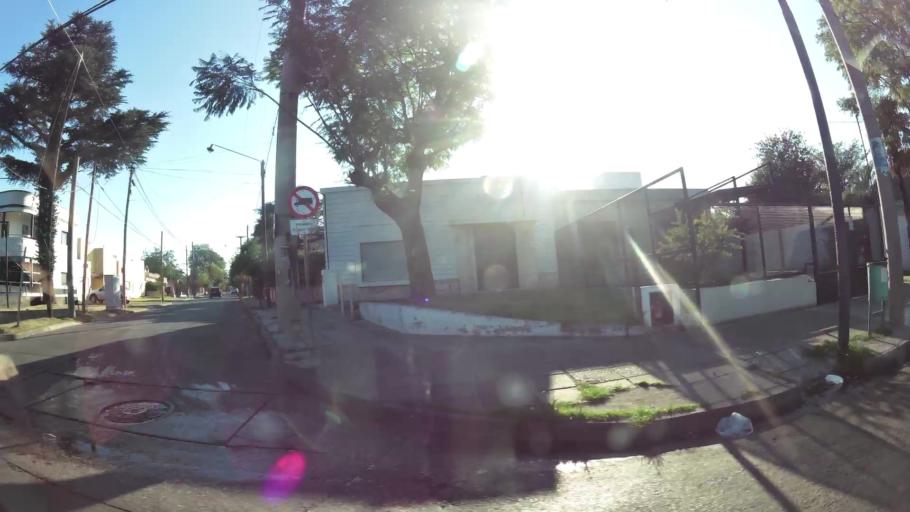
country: AR
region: Cordoba
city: Villa Allende
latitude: -31.3500
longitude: -64.2483
